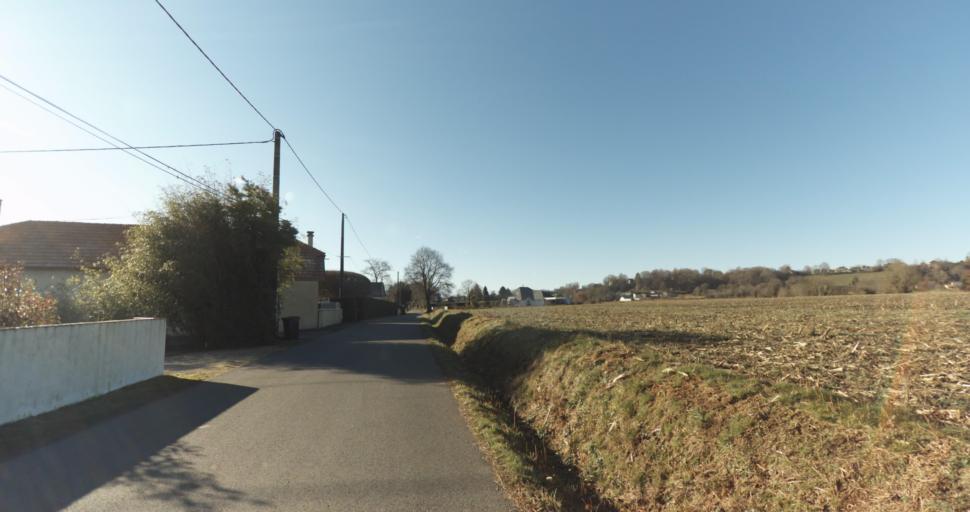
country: FR
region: Aquitaine
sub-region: Departement des Pyrenees-Atlantiques
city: Morlaas
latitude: 43.3322
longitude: -0.2498
